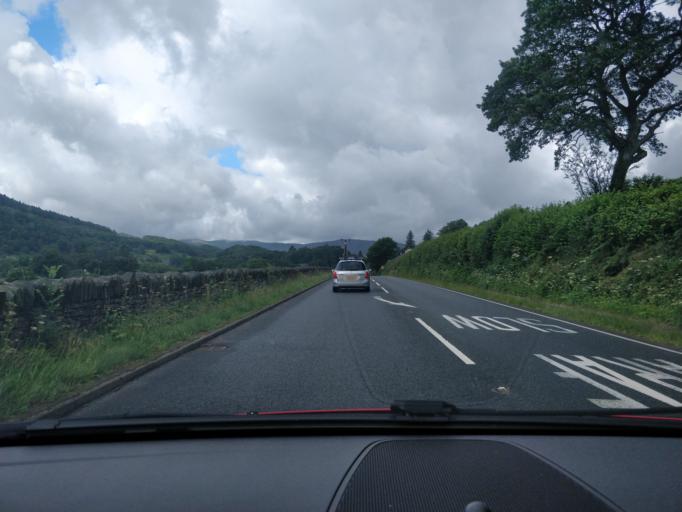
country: GB
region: Wales
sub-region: Conwy
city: Betws-y-Coed
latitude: 53.0555
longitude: -3.8795
